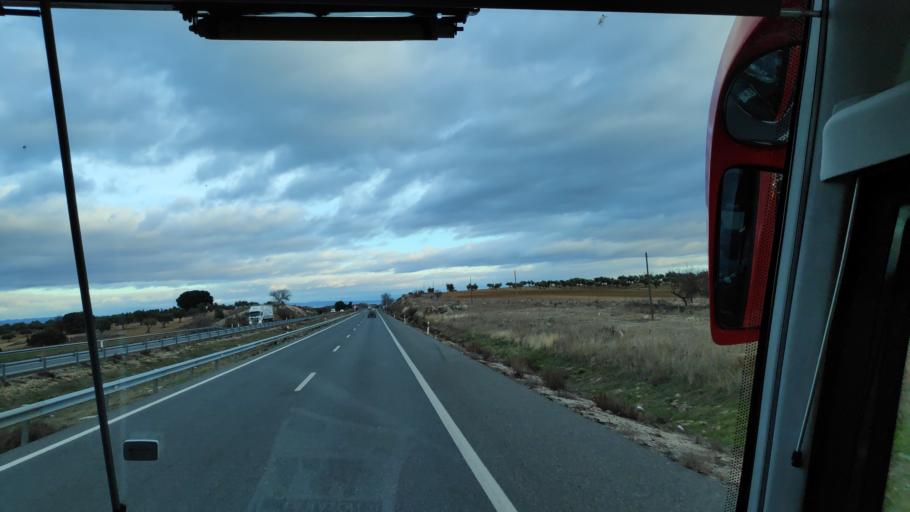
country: ES
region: Madrid
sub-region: Provincia de Madrid
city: Villarejo de Salvanes
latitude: 40.1518
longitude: -3.2429
